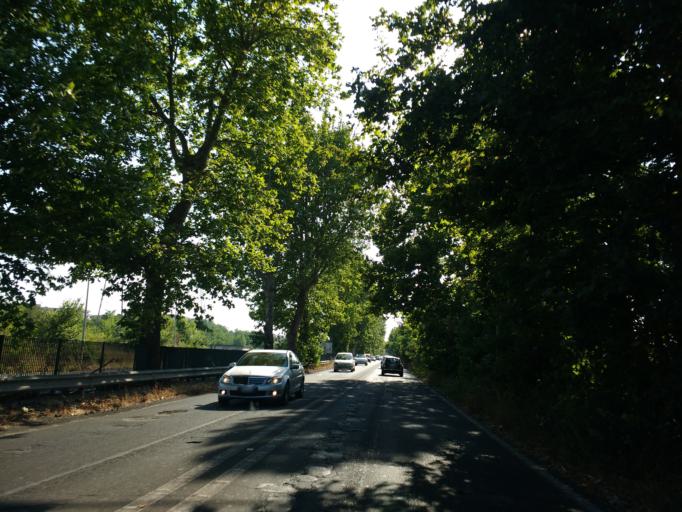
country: IT
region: Latium
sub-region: Citta metropolitana di Roma Capitale
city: Vitinia
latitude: 41.7945
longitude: 12.3963
